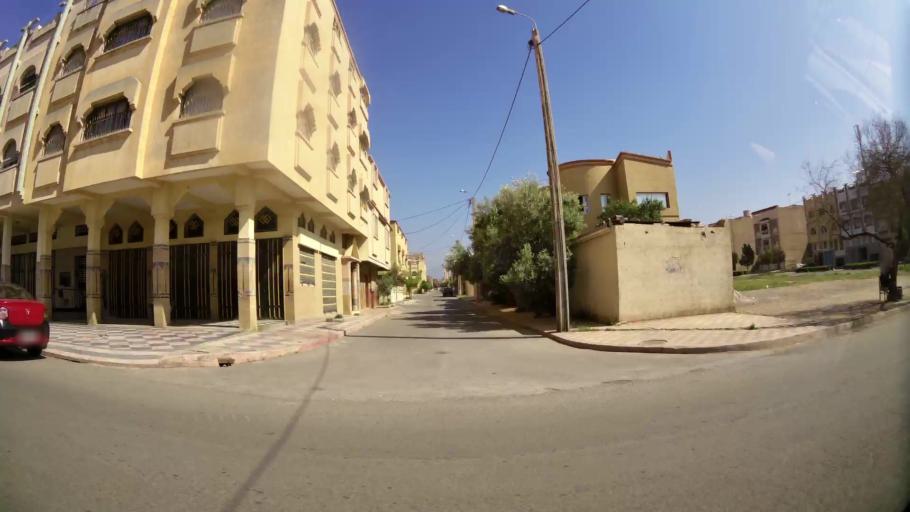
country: MA
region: Oriental
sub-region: Oujda-Angad
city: Oujda
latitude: 34.6898
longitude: -1.8768
